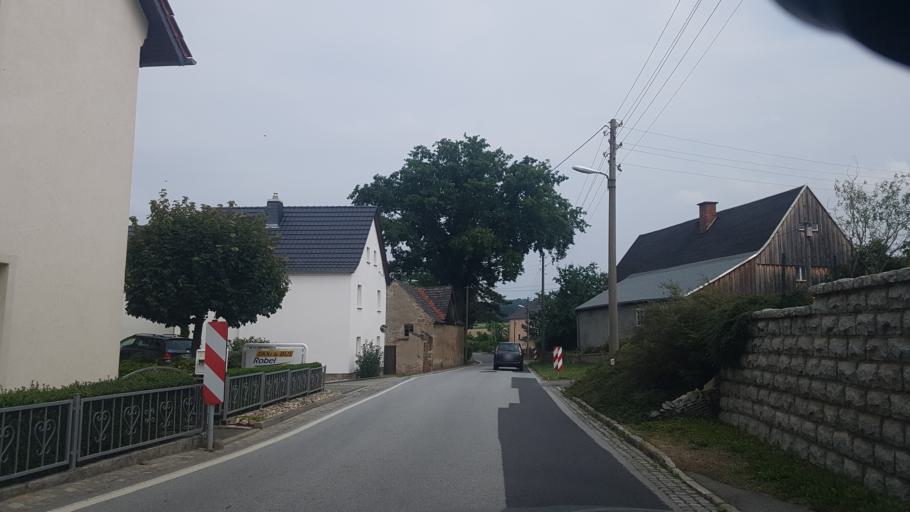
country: DE
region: Saxony
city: Crostwitz
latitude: 51.2392
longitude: 14.2461
